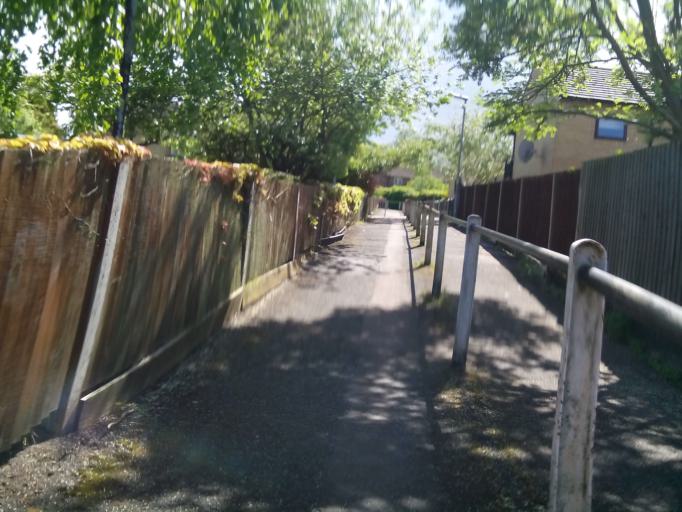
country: GB
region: England
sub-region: Cambridgeshire
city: Cambridge
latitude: 52.1847
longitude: 0.1628
